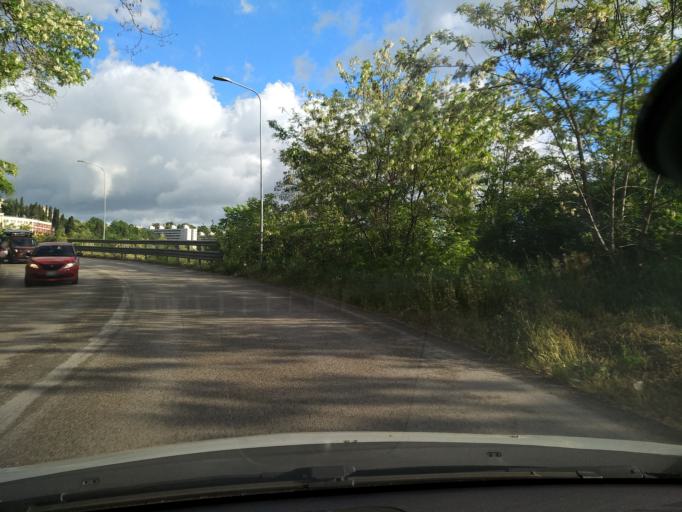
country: IT
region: The Marches
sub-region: Provincia di Pesaro e Urbino
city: Urbino
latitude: 43.7305
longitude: 12.6383
